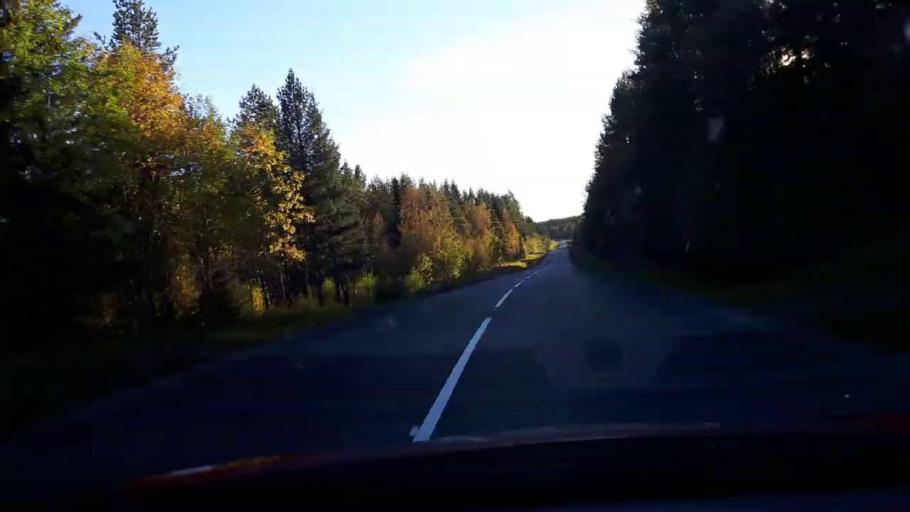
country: SE
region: Jaemtland
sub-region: OEstersunds Kommun
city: Lit
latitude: 63.4661
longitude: 14.8707
